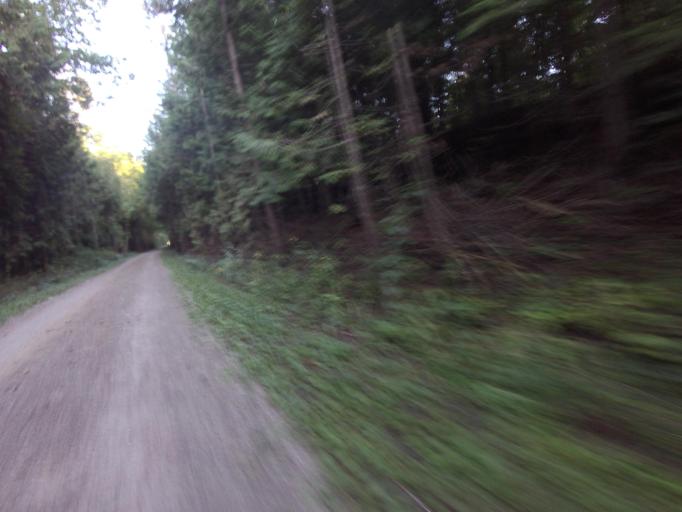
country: CA
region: Ontario
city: Goderich
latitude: 43.7602
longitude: -81.6934
